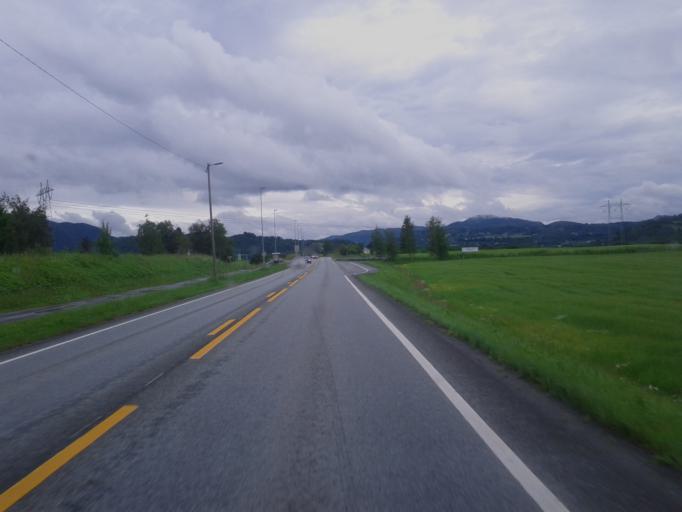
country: NO
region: Sor-Trondelag
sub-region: Melhus
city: Melhus
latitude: 63.3105
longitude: 10.2922
